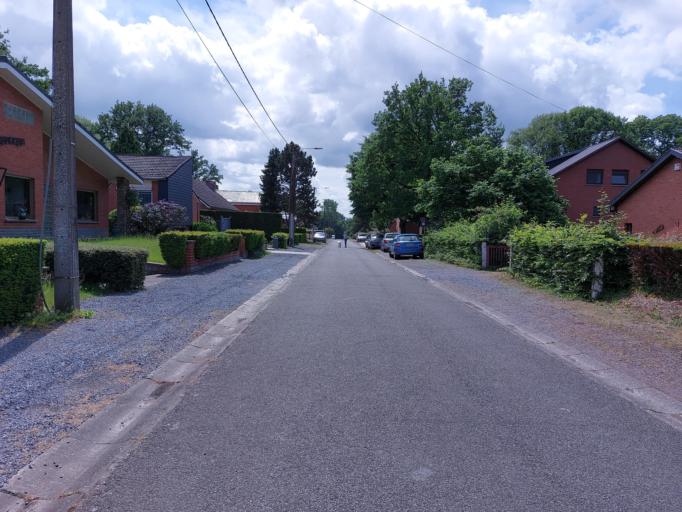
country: BE
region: Wallonia
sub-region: Province du Hainaut
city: Saint-Ghislain
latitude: 50.4898
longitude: 3.8282
